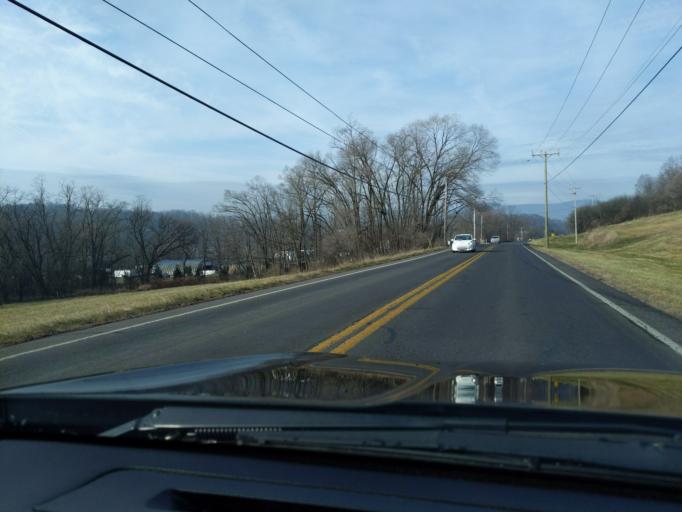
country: US
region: Pennsylvania
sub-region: Blair County
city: Duncansville
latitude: 40.4387
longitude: -78.4184
